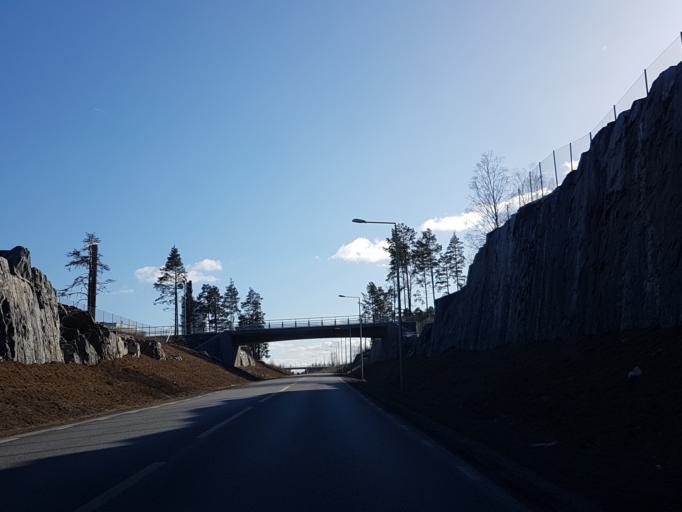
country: SE
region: Stockholm
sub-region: Norrtalje Kommun
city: Norrtalje
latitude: 59.7535
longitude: 18.6843
